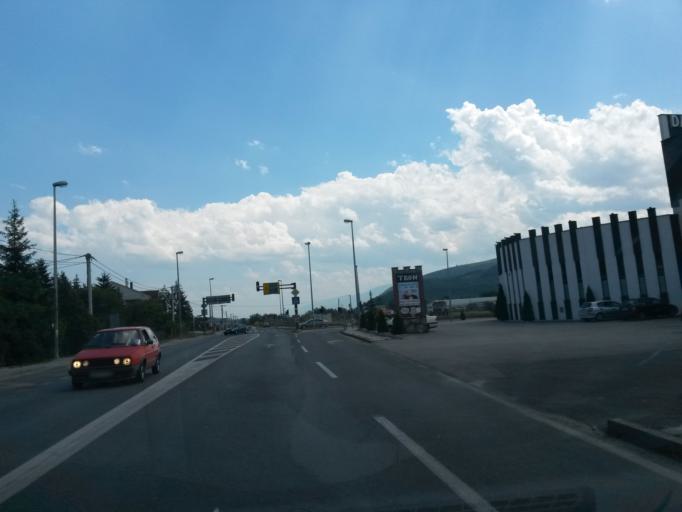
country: BA
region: Federation of Bosnia and Herzegovina
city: Travnik
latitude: 44.2074
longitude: 17.7151
